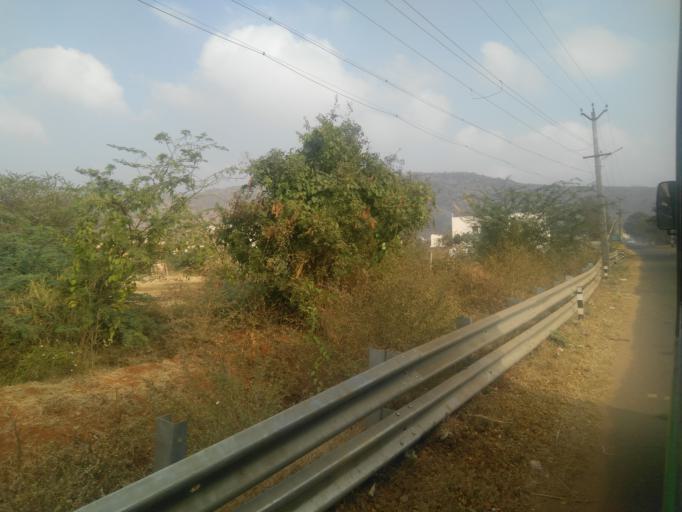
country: IN
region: Tamil Nadu
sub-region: Coimbatore
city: Perur
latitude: 11.0504
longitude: 76.8970
